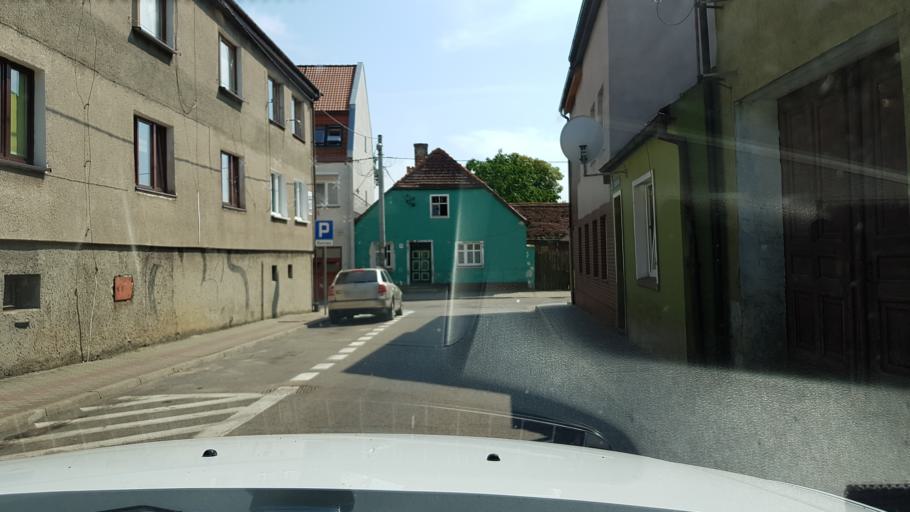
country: PL
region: West Pomeranian Voivodeship
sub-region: Powiat pyrzycki
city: Lipiany
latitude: 53.0020
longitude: 14.9713
